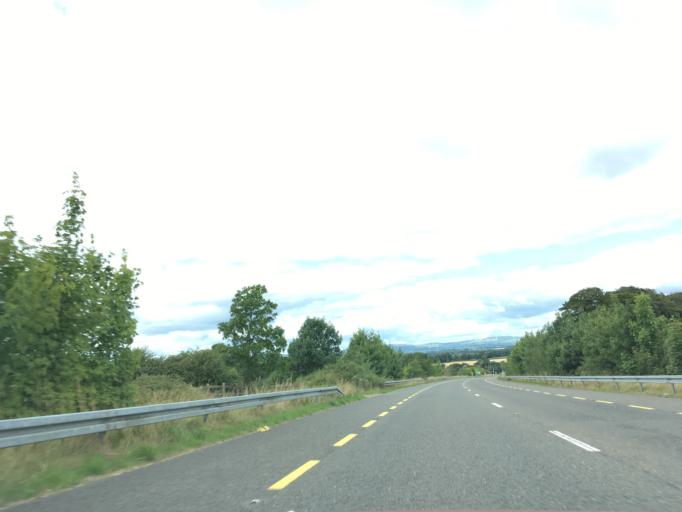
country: IE
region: Munster
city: Cashel
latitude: 52.5084
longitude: -7.9082
